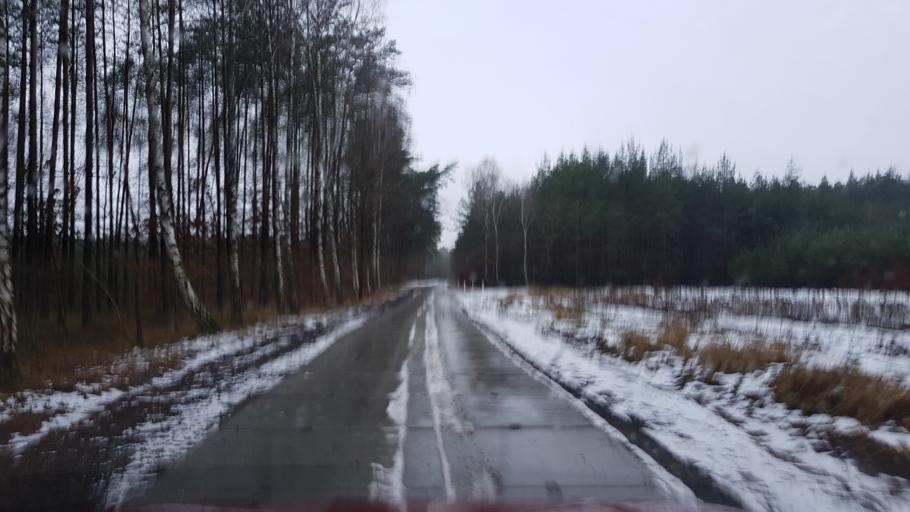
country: PL
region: West Pomeranian Voivodeship
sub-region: Powiat policki
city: Dobra
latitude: 53.5483
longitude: 14.4363
